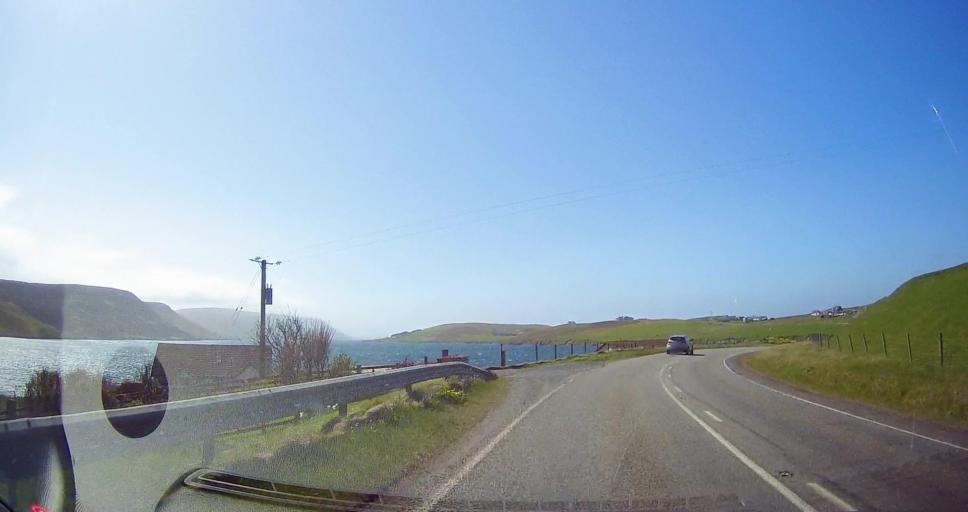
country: GB
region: Scotland
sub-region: Shetland Islands
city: Sandwick
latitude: 60.1277
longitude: -1.2773
